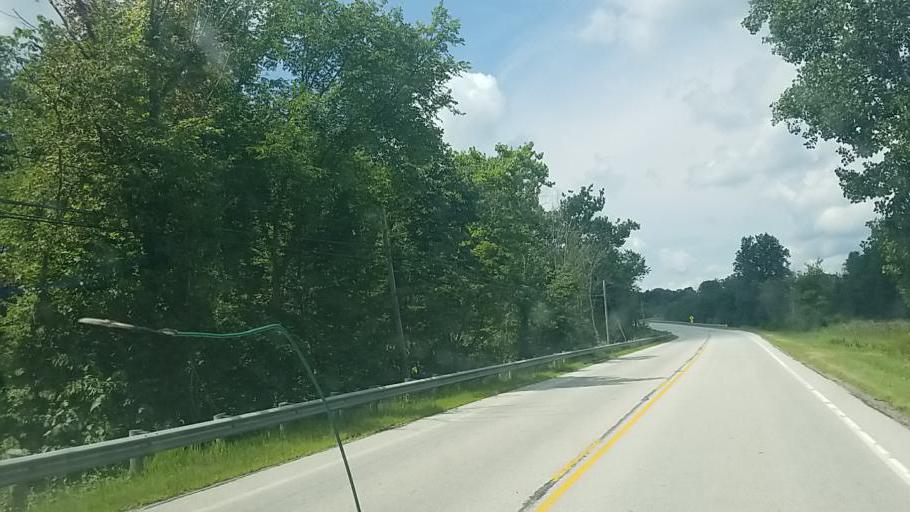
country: US
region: Ohio
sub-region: Wayne County
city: West Salem
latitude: 41.0275
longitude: -82.0915
